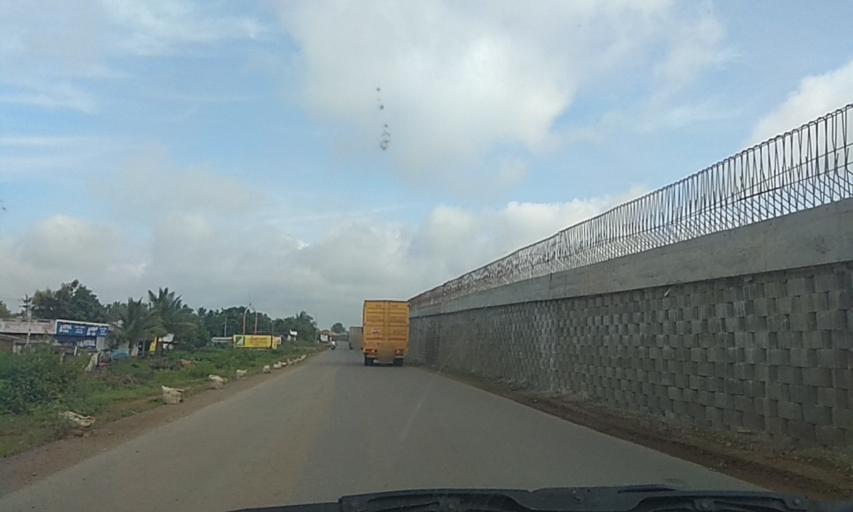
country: IN
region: Karnataka
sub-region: Haveri
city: Savanur
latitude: 14.8698
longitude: 75.3190
